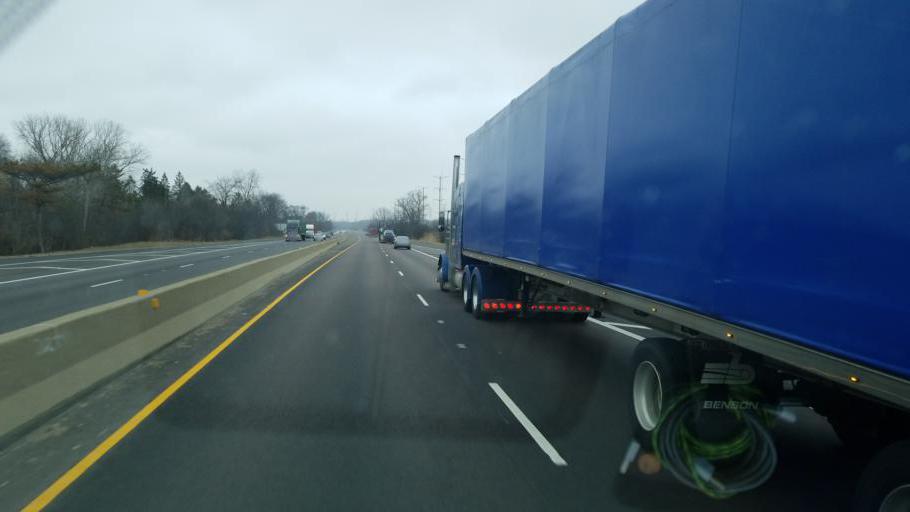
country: US
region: Illinois
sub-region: Lake County
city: Lake Forest
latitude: 42.2489
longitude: -87.8622
